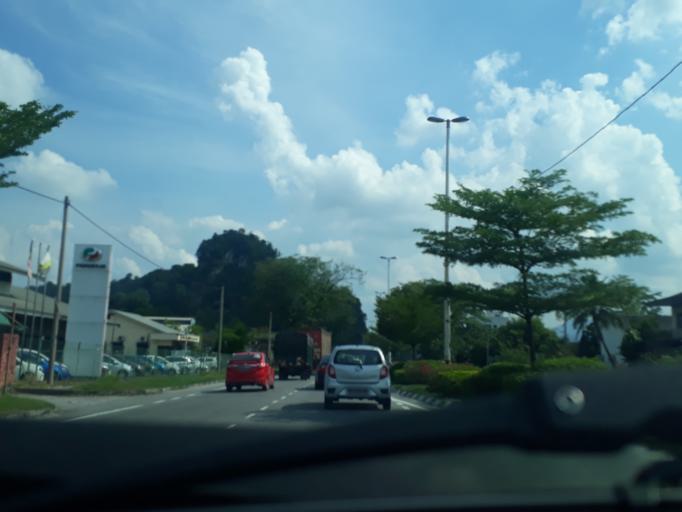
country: MY
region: Perak
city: Ipoh
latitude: 4.6486
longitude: 101.1028
